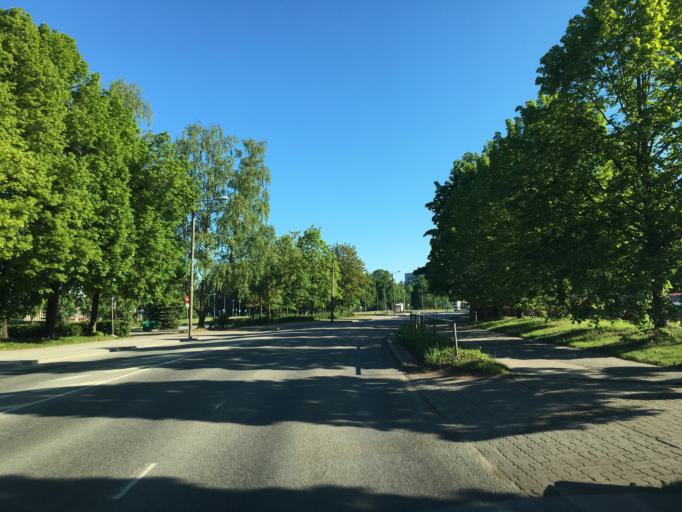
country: EE
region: Tartu
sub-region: Tartu linn
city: Tartu
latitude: 58.3845
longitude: 26.7265
